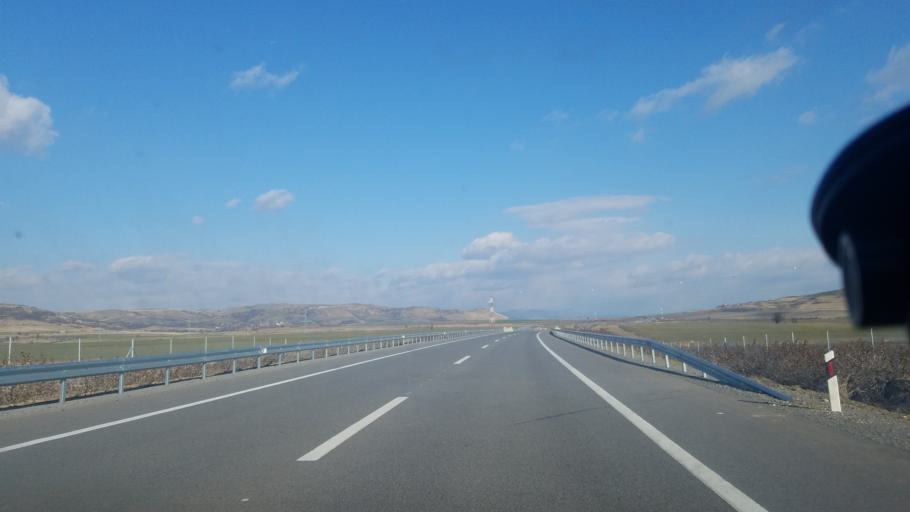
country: MK
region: Karbinci
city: Karbinci
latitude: 41.8136
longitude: 22.1748
